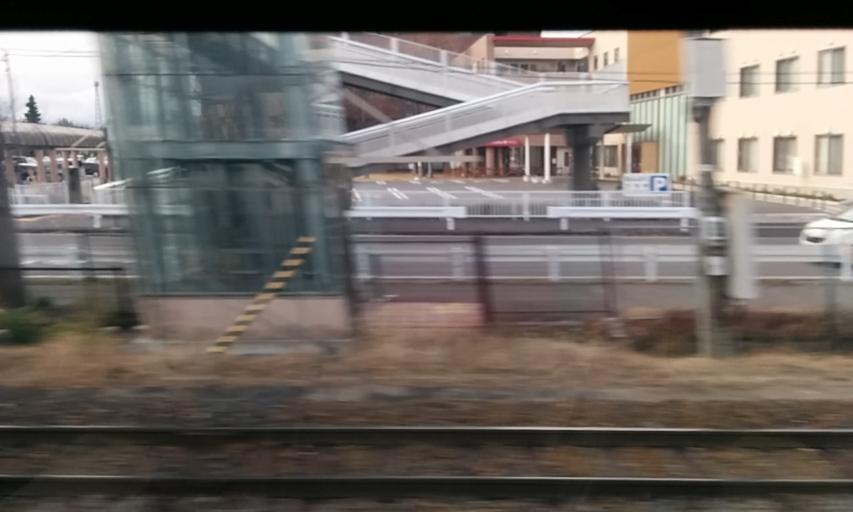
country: JP
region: Nagano
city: Matsumoto
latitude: 36.2077
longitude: 137.9685
